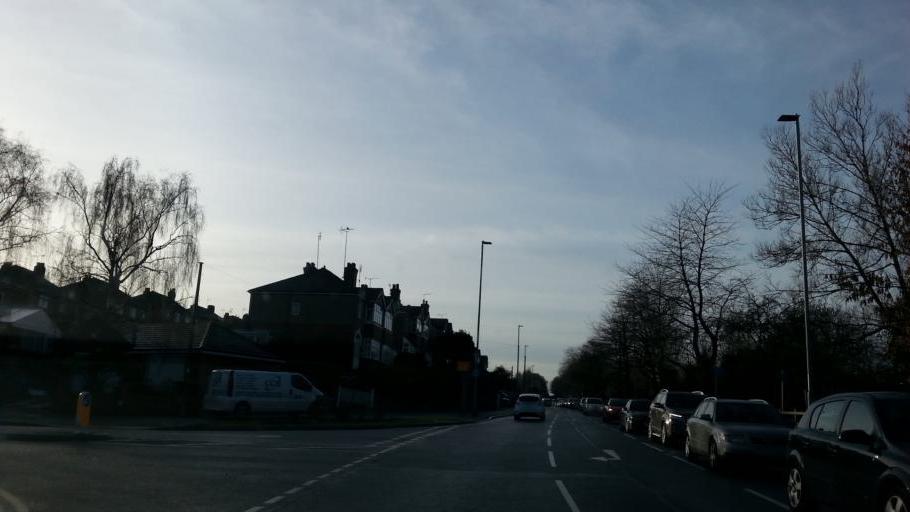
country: GB
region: England
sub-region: Stoke-on-Trent
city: Stoke-on-Trent
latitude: 53.0471
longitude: -2.1637
